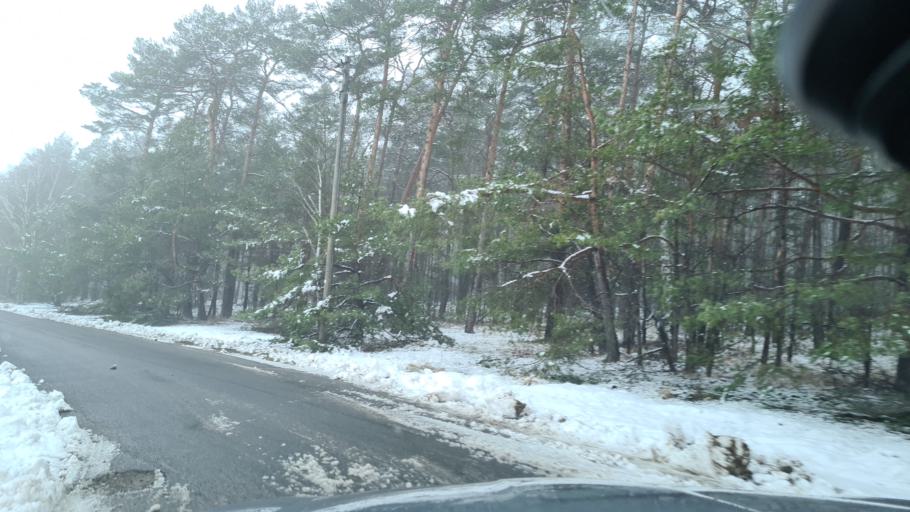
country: DE
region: Brandenburg
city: Bad Liebenwerda
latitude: 51.5293
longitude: 13.4511
